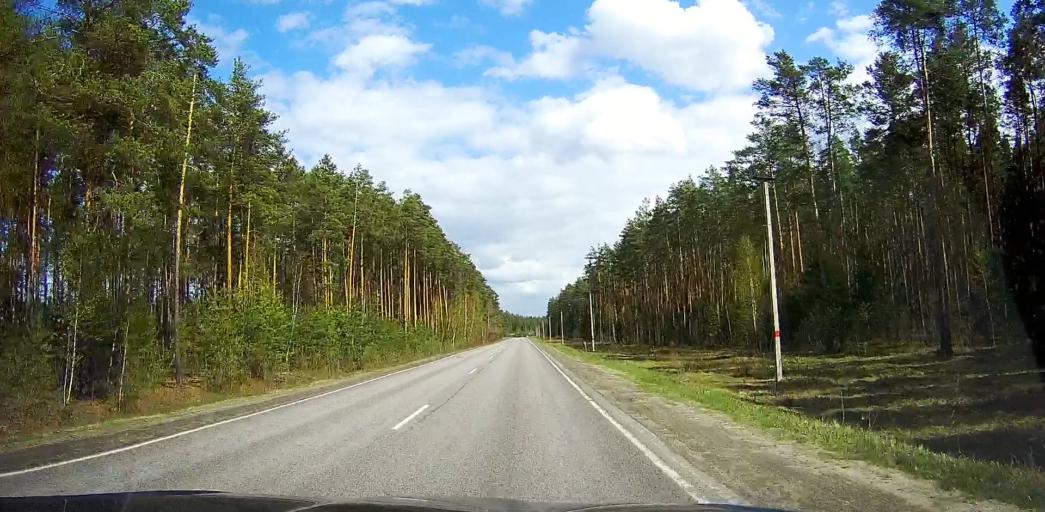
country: RU
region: Moskovskaya
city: Davydovo
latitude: 55.5547
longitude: 38.8250
